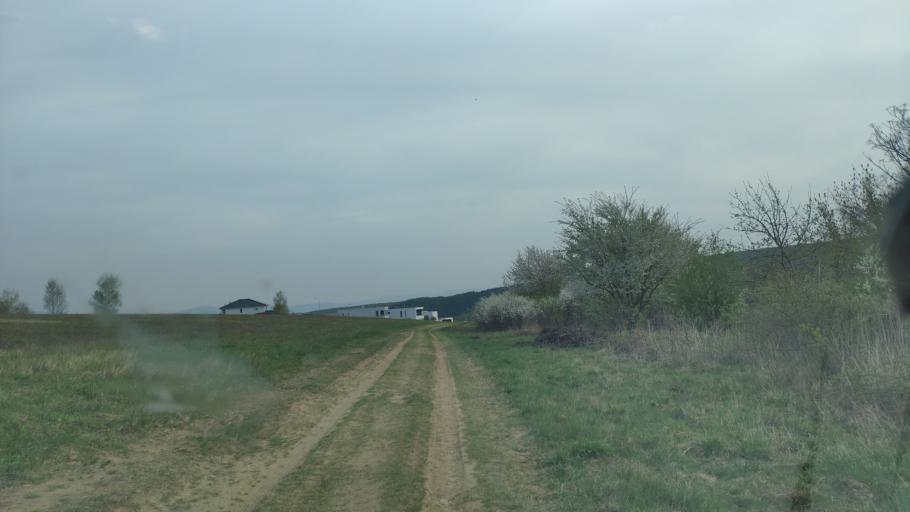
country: SK
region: Kosicky
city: Kosice
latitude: 48.7196
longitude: 21.1982
